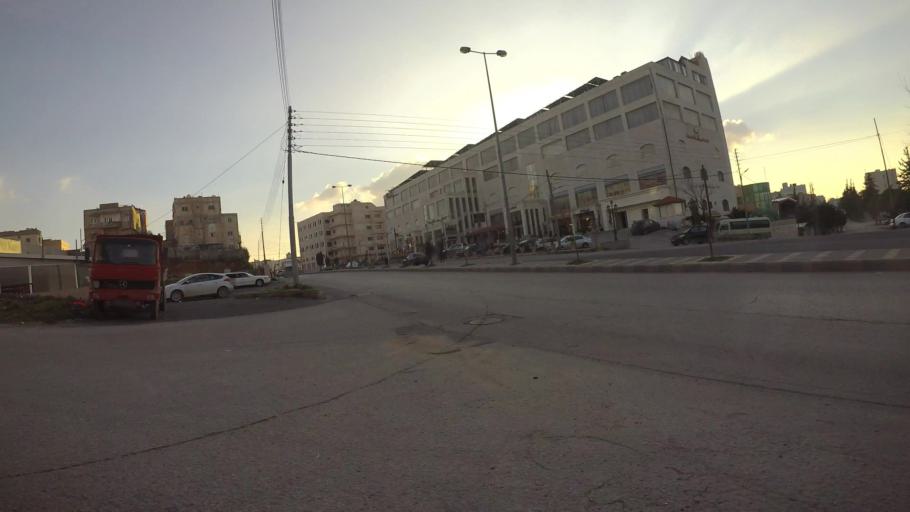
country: JO
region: Amman
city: Al Bunayyat ash Shamaliyah
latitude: 31.9114
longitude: 35.9144
